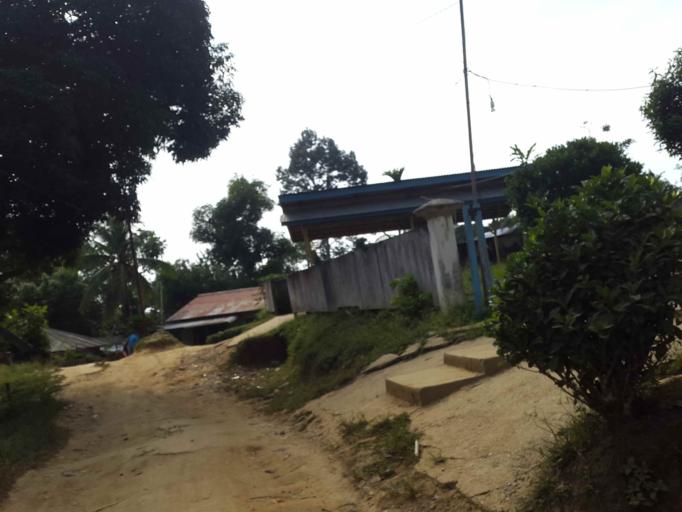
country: MY
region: Sarawak
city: Simanggang
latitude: 0.6895
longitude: 111.5191
